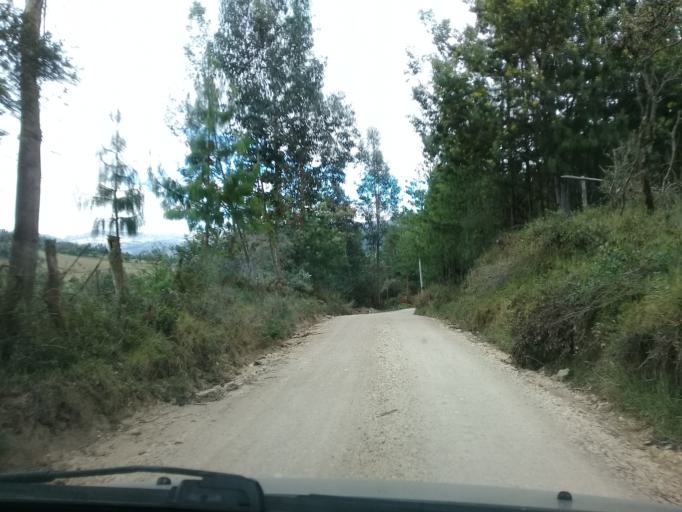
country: CO
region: Cundinamarca
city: Lenguazaque
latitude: 5.2907
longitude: -73.7235
